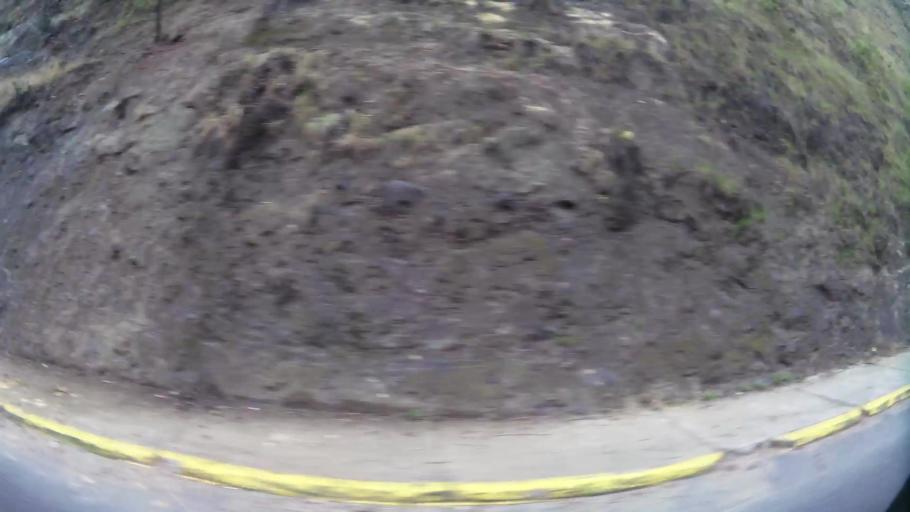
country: EC
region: Pichincha
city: Quito
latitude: -0.2337
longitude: -78.5028
